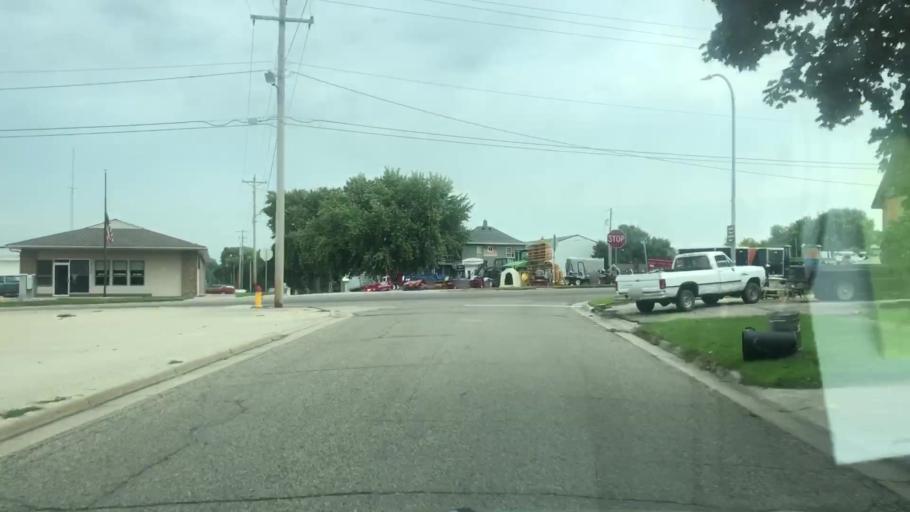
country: US
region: Iowa
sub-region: O'Brien County
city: Sheldon
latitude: 43.1855
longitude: -95.8530
